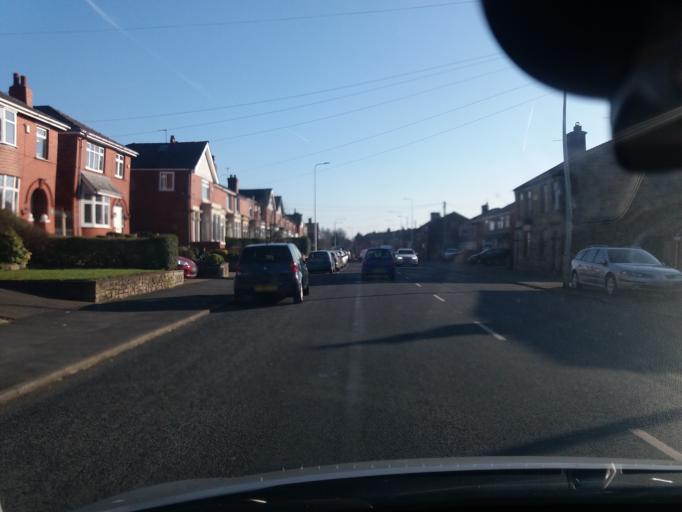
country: GB
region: England
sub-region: Lancashire
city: Adlington
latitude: 53.6238
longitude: -2.6066
